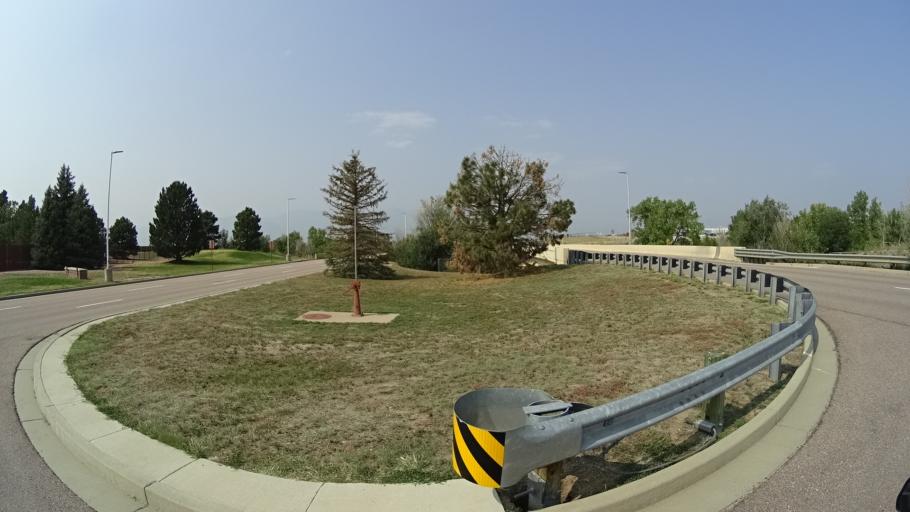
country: US
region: Colorado
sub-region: El Paso County
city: Cimarron Hills
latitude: 38.8316
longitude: -104.7111
